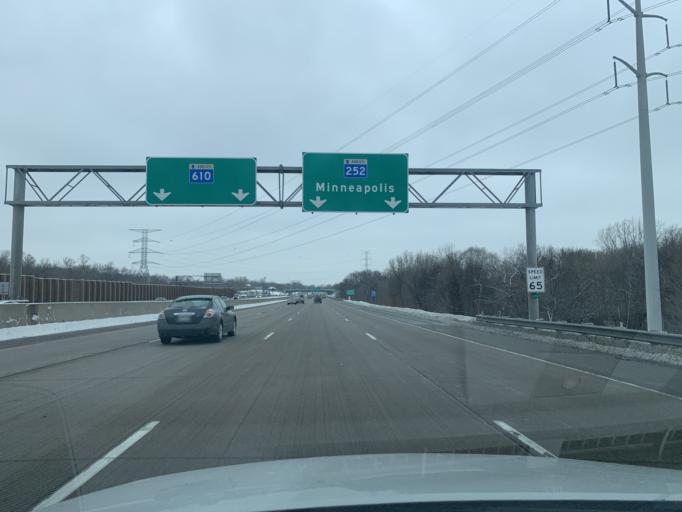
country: US
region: Minnesota
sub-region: Anoka County
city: Coon Rapids
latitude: 45.1335
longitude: -93.2959
